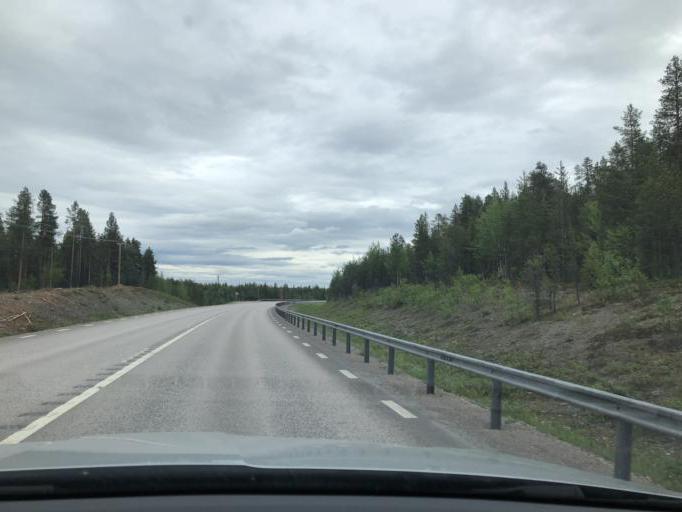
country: SE
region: Norrbotten
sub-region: Gallivare Kommun
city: Malmberget
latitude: 67.6438
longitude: 21.1083
